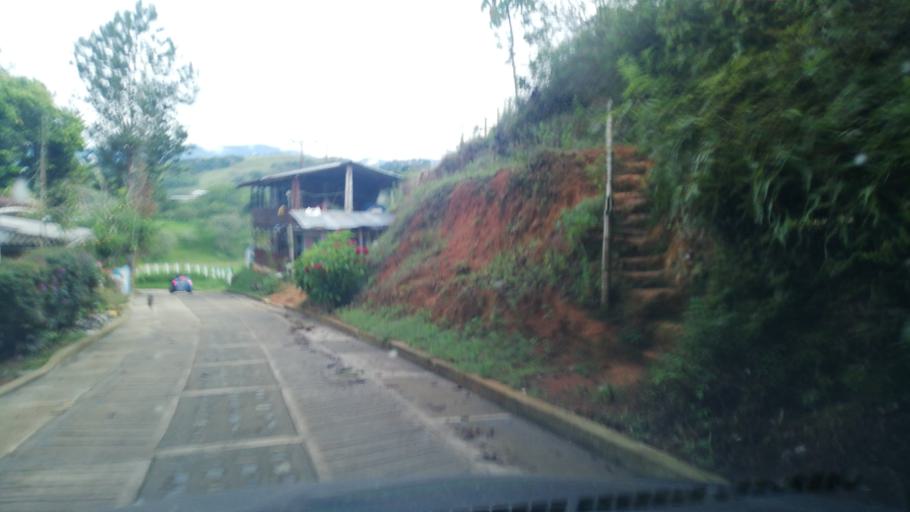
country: CO
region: Valle del Cauca
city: Restrepo
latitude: 3.8517
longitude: -76.4572
